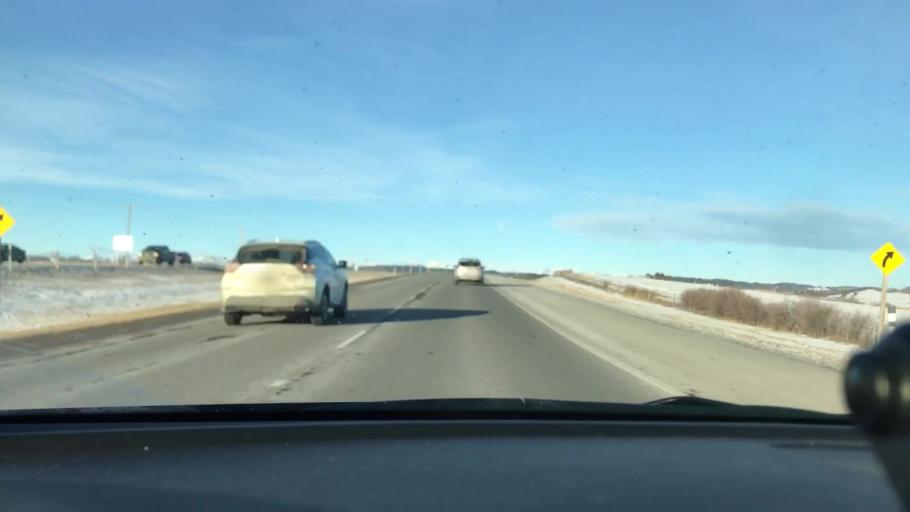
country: CA
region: Alberta
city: Cochrane
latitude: 51.1119
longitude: -114.6448
